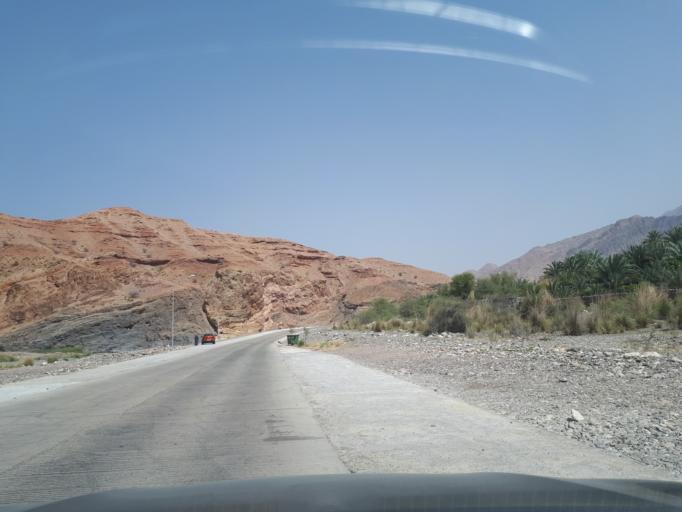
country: OM
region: Ash Sharqiyah
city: Ibra'
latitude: 23.0895
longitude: 58.8647
